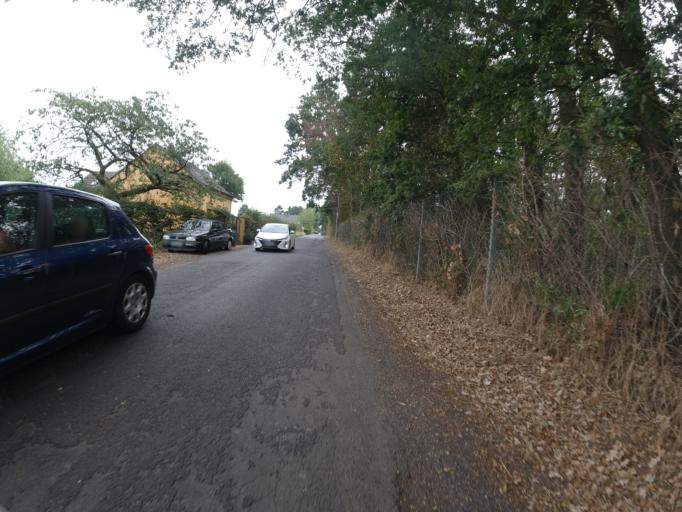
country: DE
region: North Rhine-Westphalia
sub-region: Regierungsbezirk Dusseldorf
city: Moers
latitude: 51.3947
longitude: 6.6210
